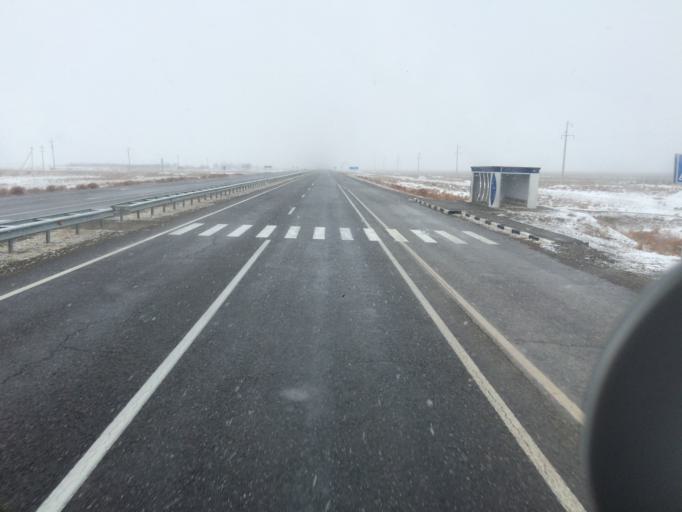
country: KZ
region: Ongtustik Qazaqstan
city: Turkestan
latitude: 43.4578
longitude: 67.9324
